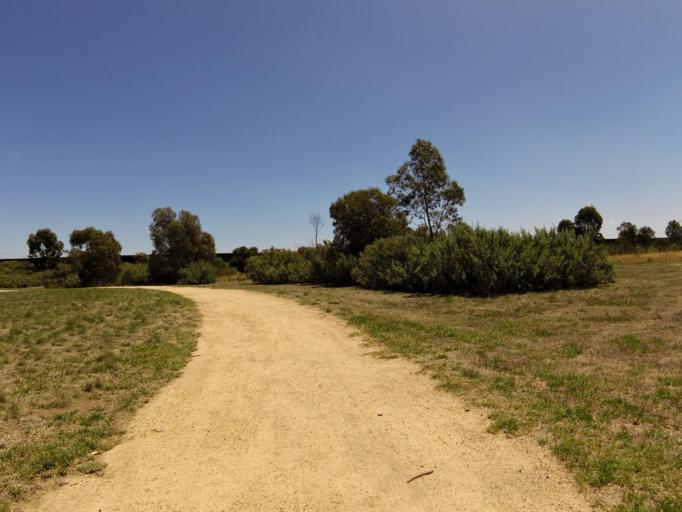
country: AU
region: Victoria
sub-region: Whittlesea
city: Lalor
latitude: -37.6673
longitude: 144.9830
